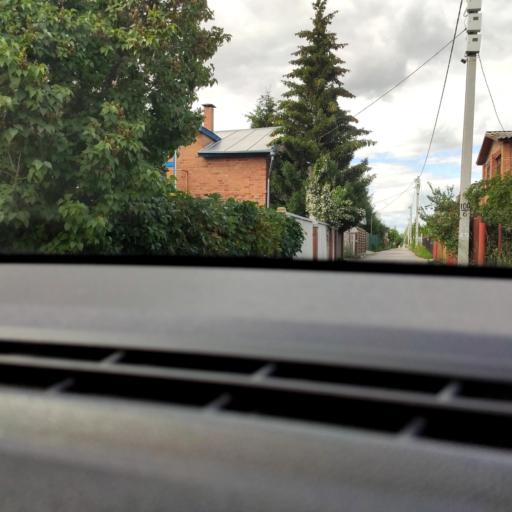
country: RU
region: Samara
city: Podstepki
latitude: 53.5793
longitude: 49.0731
